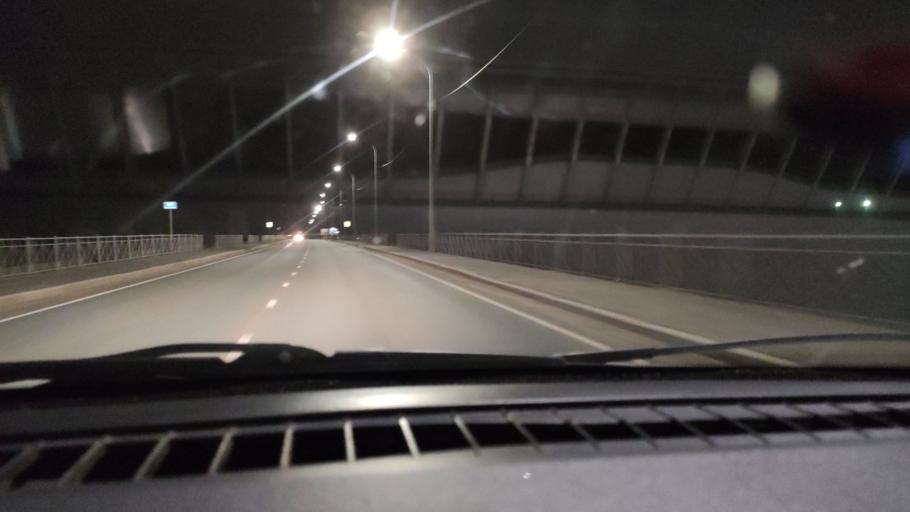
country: RU
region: Bashkortostan
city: Yermolayevo
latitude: 52.5926
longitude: 55.8494
